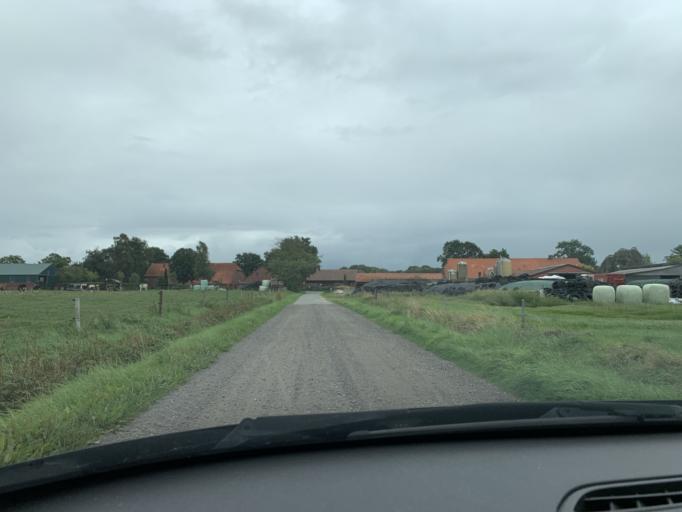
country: DE
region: Lower Saxony
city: Westerstede
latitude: 53.2447
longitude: 7.8847
